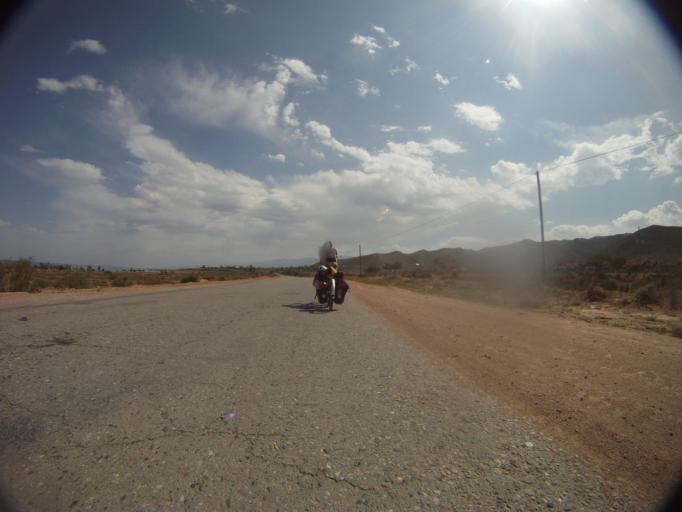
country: KG
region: Ysyk-Koel
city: Kadzhi-Say
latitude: 42.1719
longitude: 77.3679
